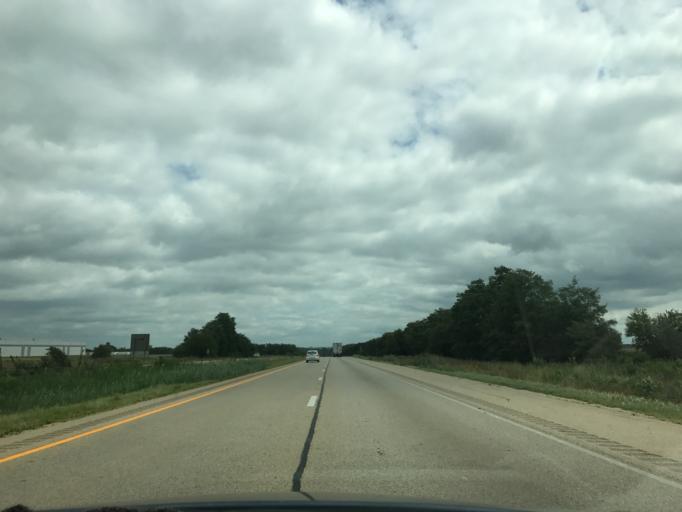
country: US
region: Illinois
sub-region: LaSalle County
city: Ottawa
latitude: 41.3762
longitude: -88.8253
